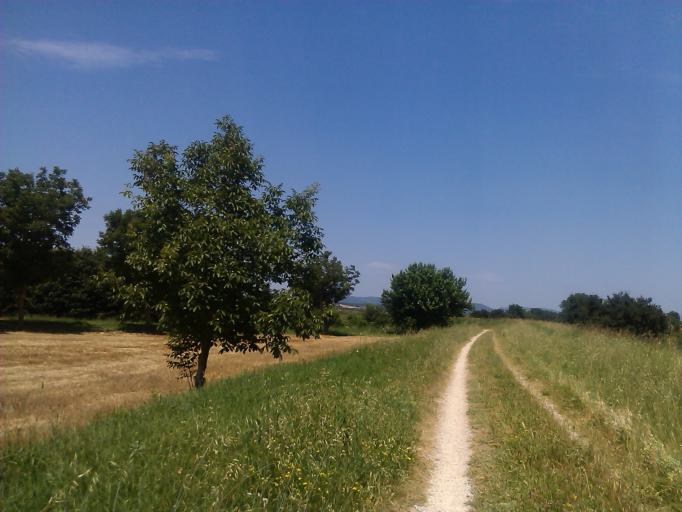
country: IT
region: Tuscany
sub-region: Province of Arezzo
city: Cesa
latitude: 43.3146
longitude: 11.8385
